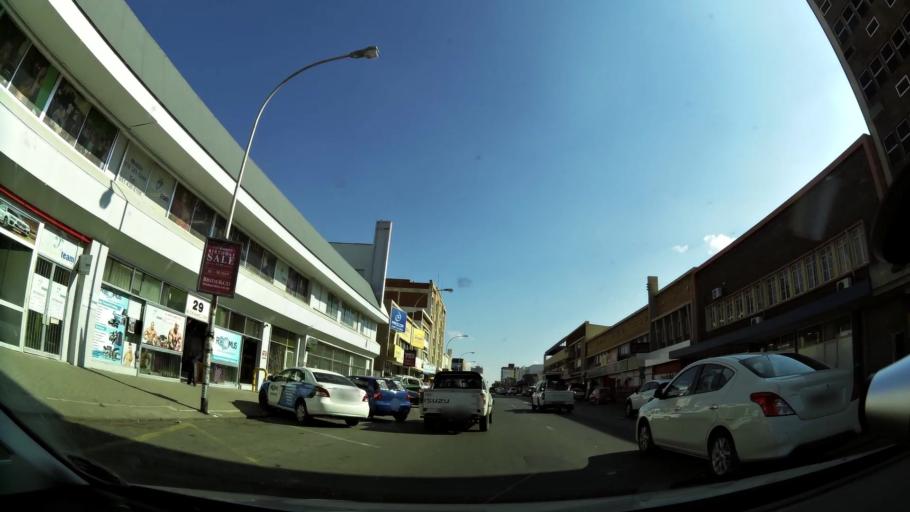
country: ZA
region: Orange Free State
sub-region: Mangaung Metropolitan Municipality
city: Bloemfontein
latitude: -29.1148
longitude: 26.2239
